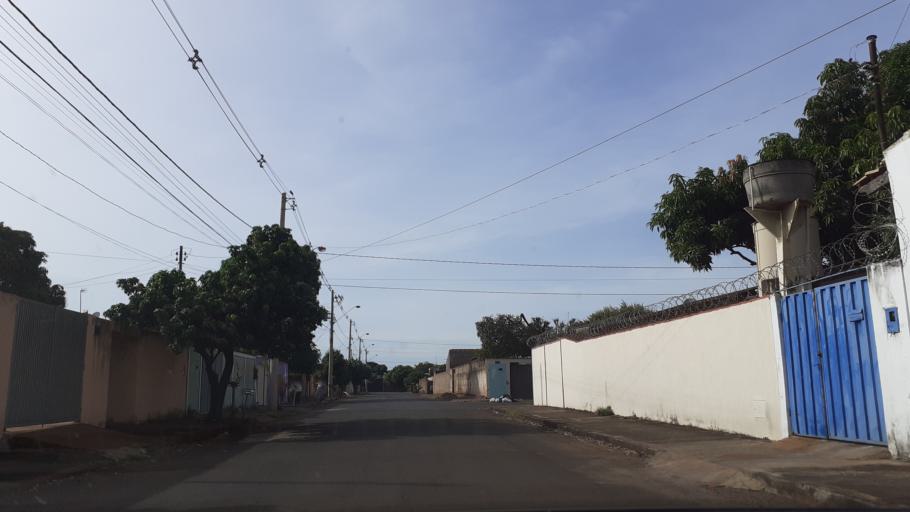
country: BR
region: Goias
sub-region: Itumbiara
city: Itumbiara
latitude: -18.4165
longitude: -49.2428
